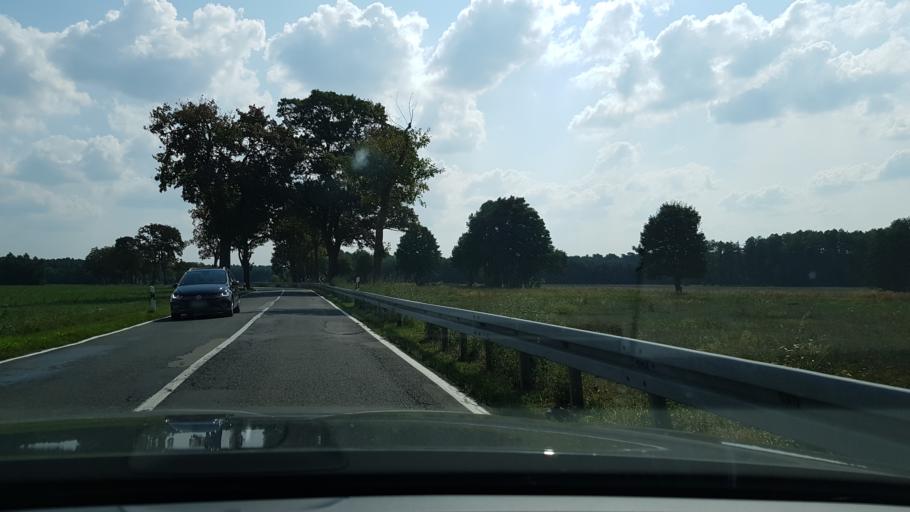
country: DE
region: Brandenburg
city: Lindow
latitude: 53.0185
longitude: 12.9756
